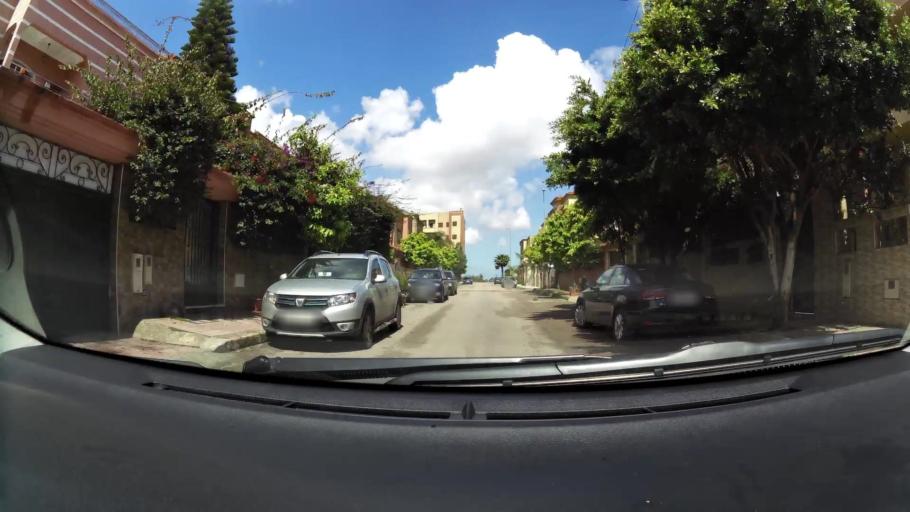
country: MA
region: Grand Casablanca
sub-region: Mediouna
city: Tit Mellil
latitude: 33.5550
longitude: -7.4839
